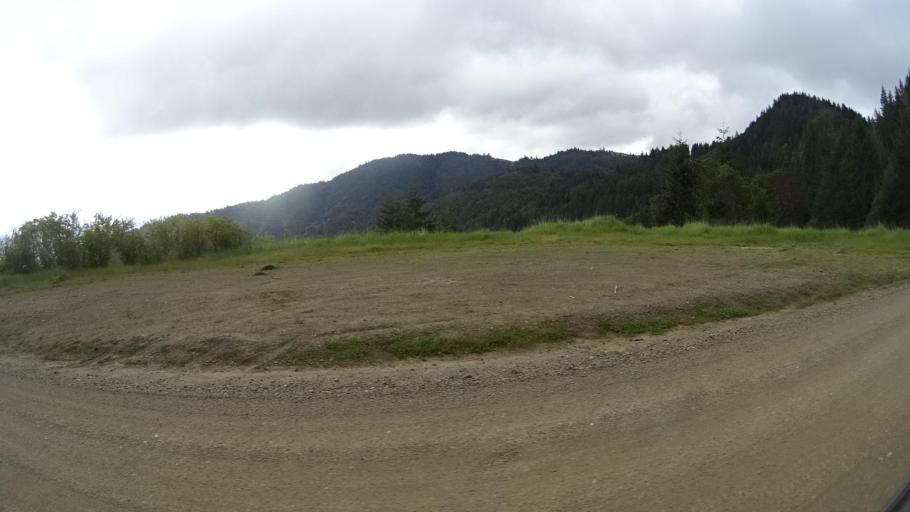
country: US
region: California
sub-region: Humboldt County
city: Redway
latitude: 40.2289
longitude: -123.7613
